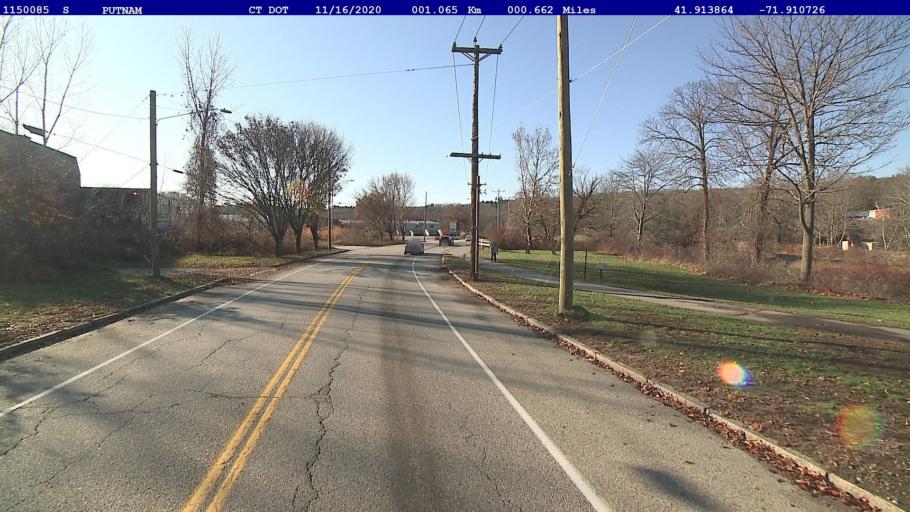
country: US
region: Connecticut
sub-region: Windham County
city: Putnam
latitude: 41.9139
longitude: -71.9107
